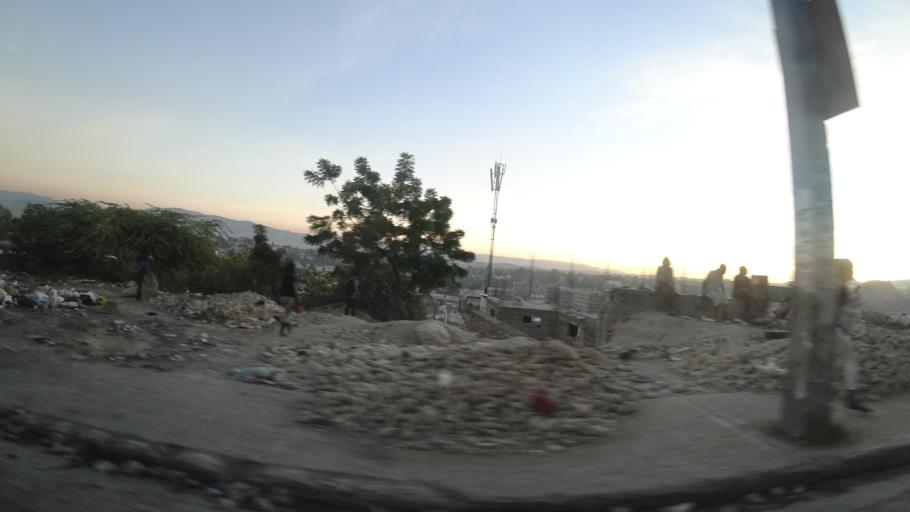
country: HT
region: Ouest
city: Delmas 73
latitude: 18.5515
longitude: -72.3173
